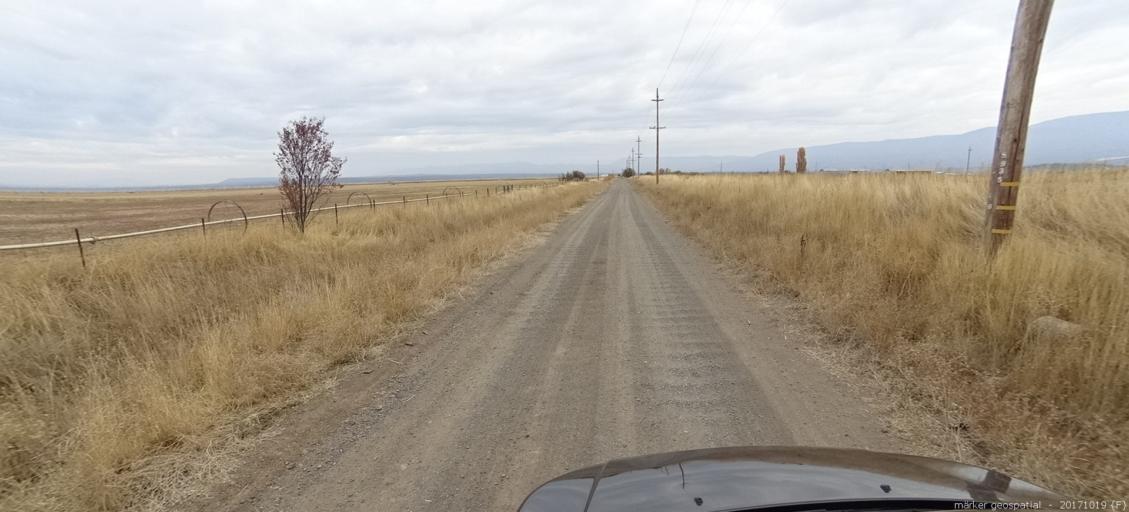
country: US
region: California
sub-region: Shasta County
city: Burney
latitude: 41.0681
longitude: -121.3891
